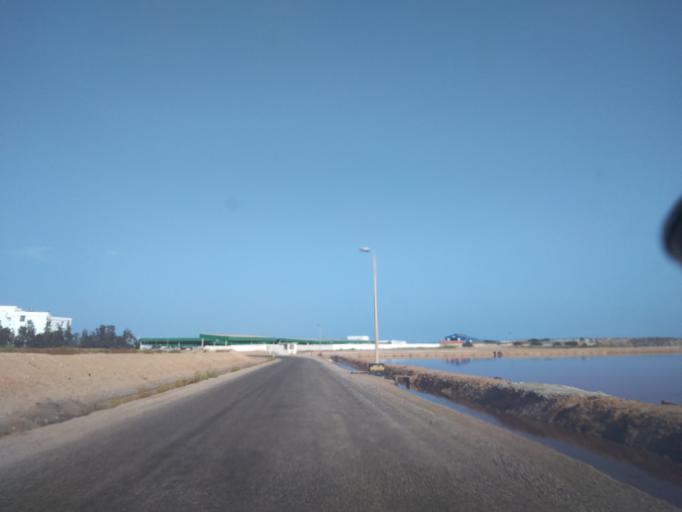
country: TN
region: Safaqis
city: Sfax
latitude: 34.7251
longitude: 10.7509
